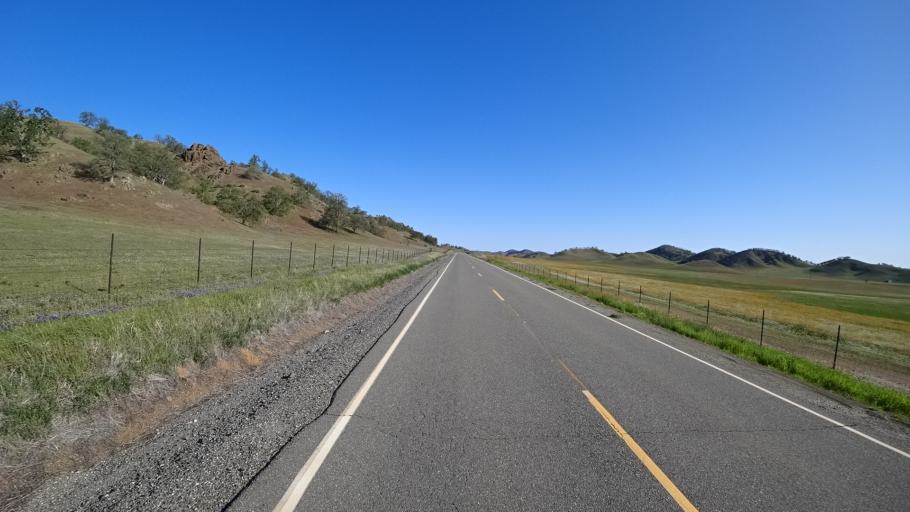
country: US
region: California
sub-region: Tehama County
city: Rancho Tehama Reserve
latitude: 39.7566
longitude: -122.5249
